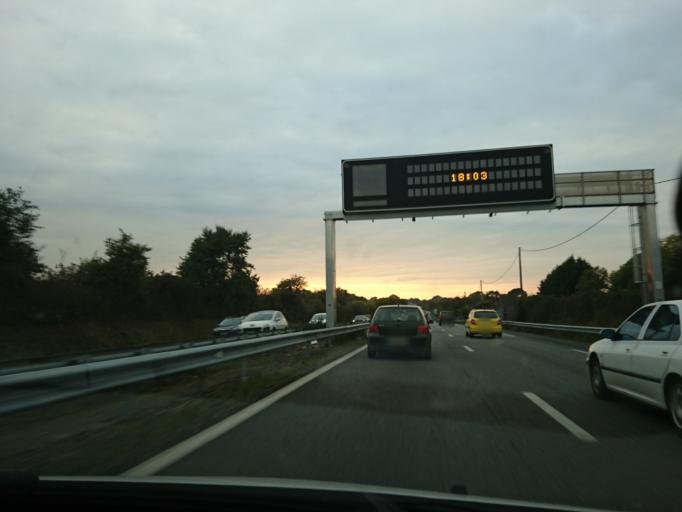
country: FR
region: Brittany
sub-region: Departement du Morbihan
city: Pluneret
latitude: 47.6716
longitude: -2.9388
